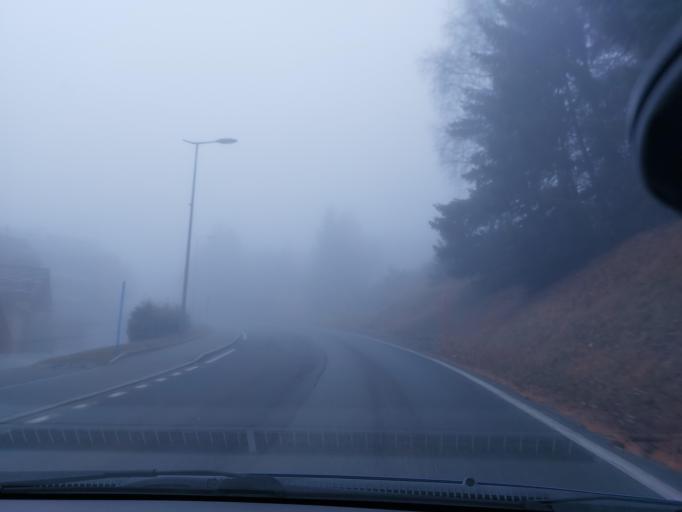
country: CH
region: Valais
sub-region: Sierre District
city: Lens
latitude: 46.3019
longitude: 7.4532
